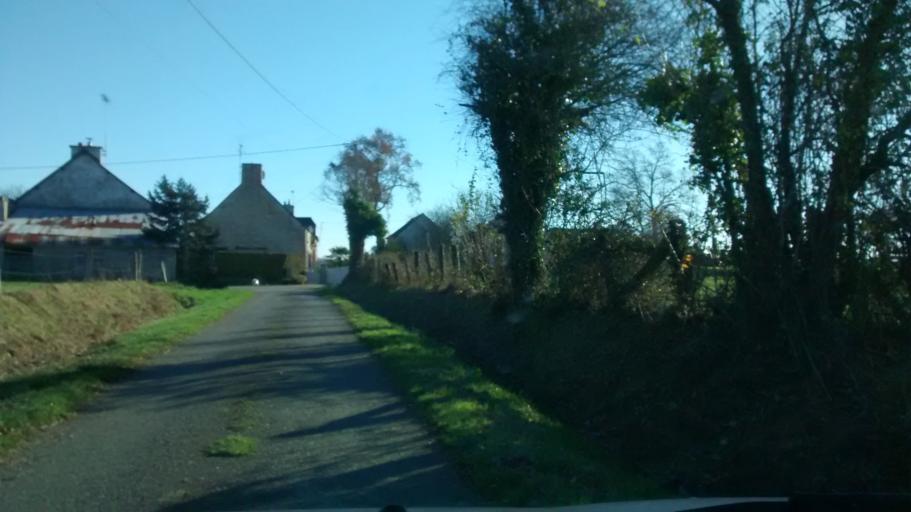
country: FR
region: Brittany
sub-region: Departement d'Ille-et-Vilaine
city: Liffre
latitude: 48.2066
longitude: -1.4696
